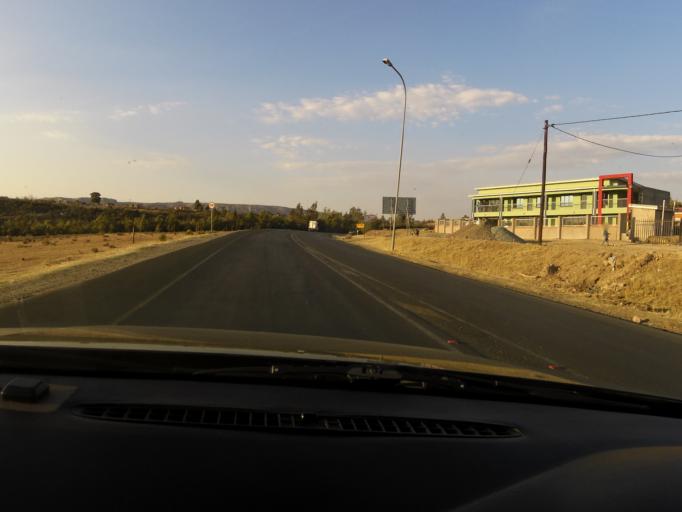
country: LS
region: Maseru
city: Maseru
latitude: -29.3904
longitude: 27.5526
